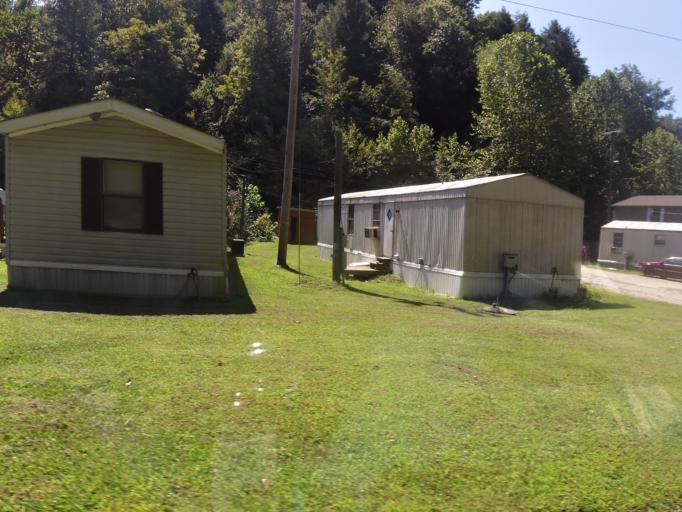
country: US
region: Kentucky
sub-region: Leslie County
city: Hyden
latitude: 37.1412
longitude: -83.4351
